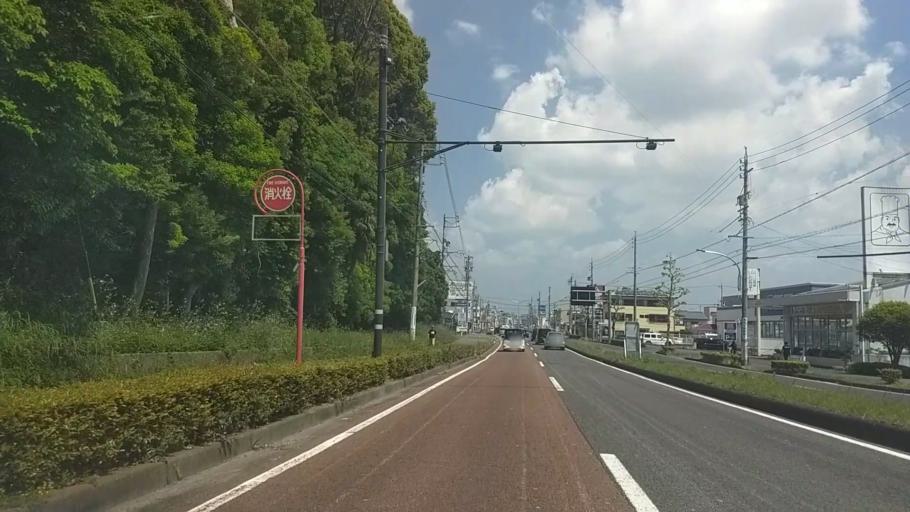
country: JP
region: Shizuoka
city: Hamamatsu
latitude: 34.7238
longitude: 137.7307
